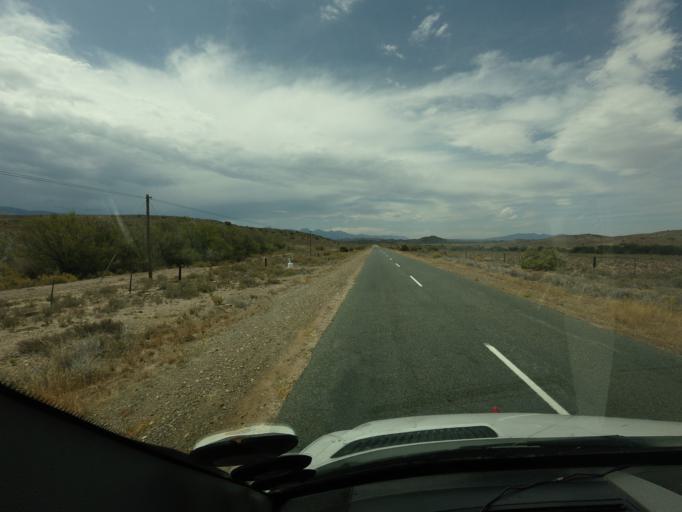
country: ZA
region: Western Cape
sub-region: Eden District Municipality
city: Ladismith
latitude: -33.6644
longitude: 20.9997
